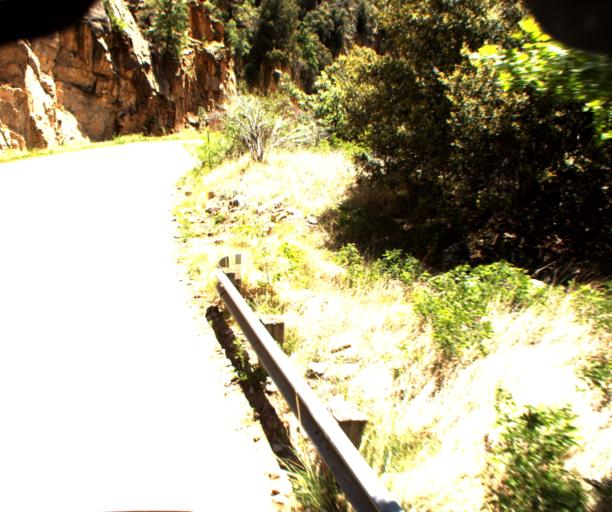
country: US
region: Arizona
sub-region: Coconino County
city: Sedona
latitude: 34.9691
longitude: -111.7498
